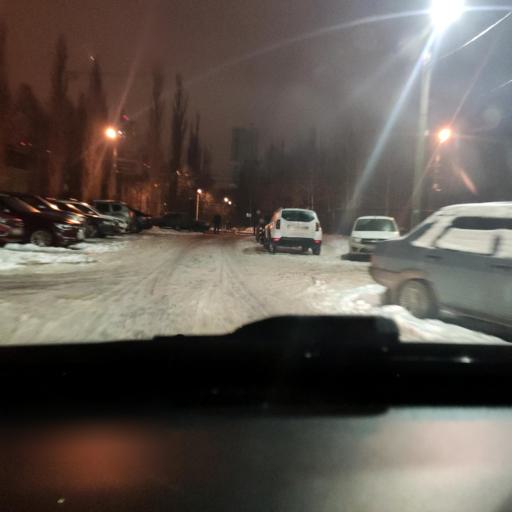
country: RU
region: Voronezj
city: Podgornoye
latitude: 51.7554
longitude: 39.1850
